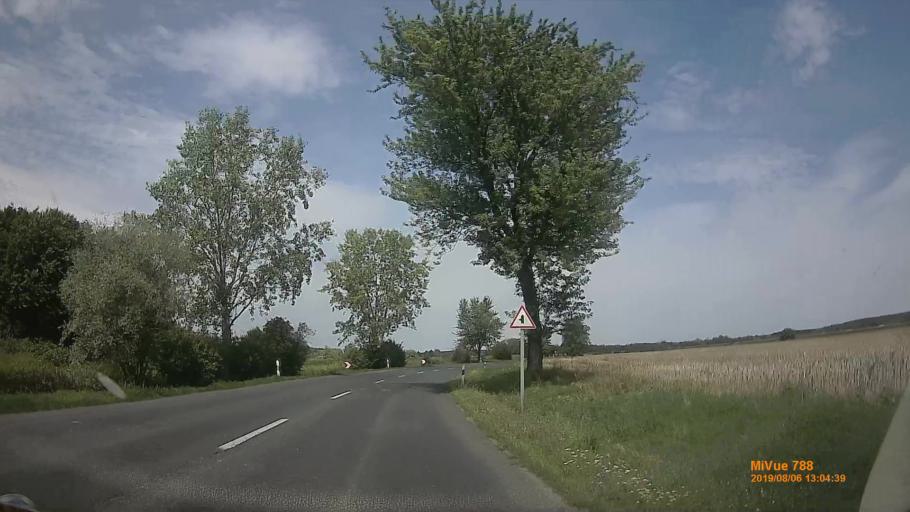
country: HU
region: Vas
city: Koszeg
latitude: 47.3554
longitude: 16.5680
